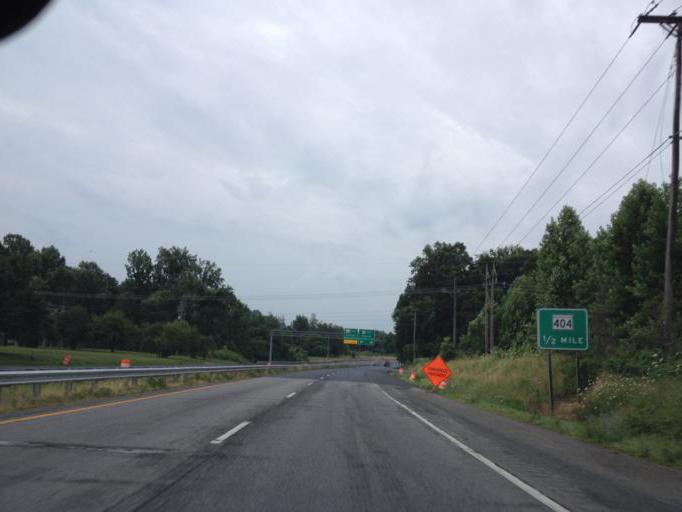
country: US
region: Maryland
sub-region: Queen Anne's County
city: Centreville
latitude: 38.9470
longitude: -76.0645
